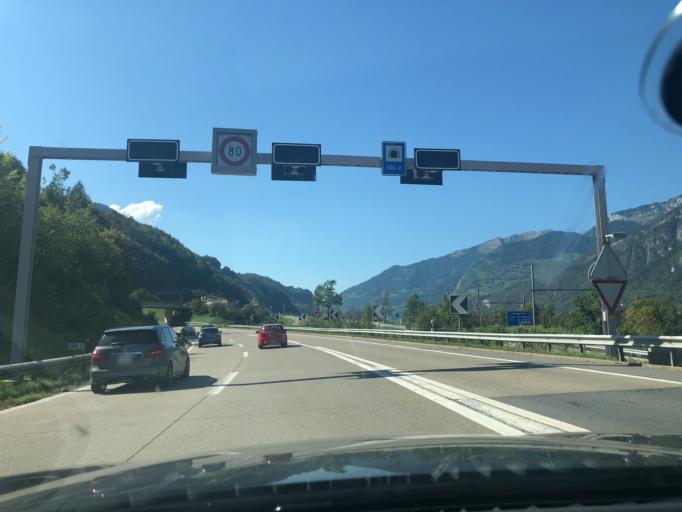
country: CH
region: Saint Gallen
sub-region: Wahlkreis Sarganserland
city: Quarten
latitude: 47.1150
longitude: 9.1917
